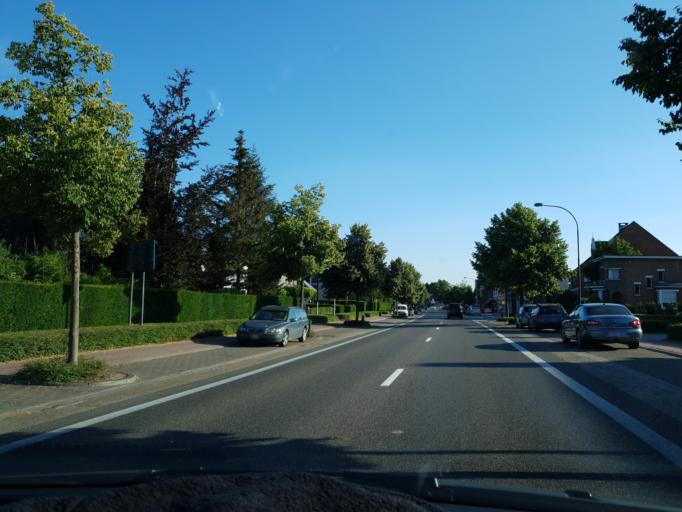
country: BE
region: Flanders
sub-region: Provincie Antwerpen
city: Hoogstraten
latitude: 51.3945
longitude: 4.7567
